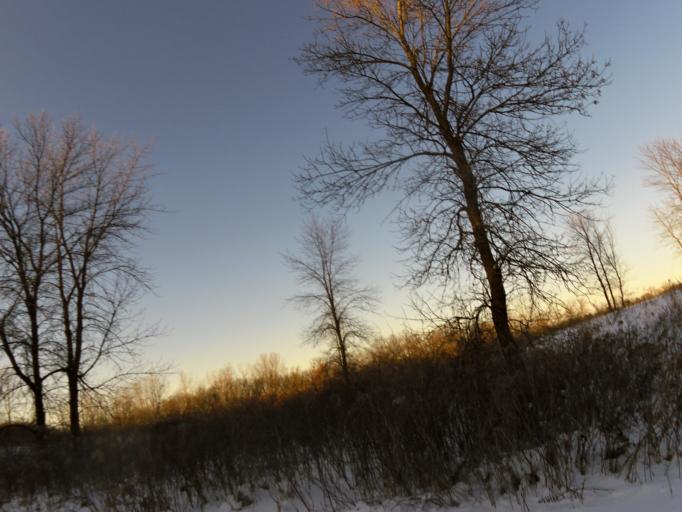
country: US
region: Minnesota
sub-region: Washington County
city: Lake Elmo
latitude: 44.9694
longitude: -92.9102
